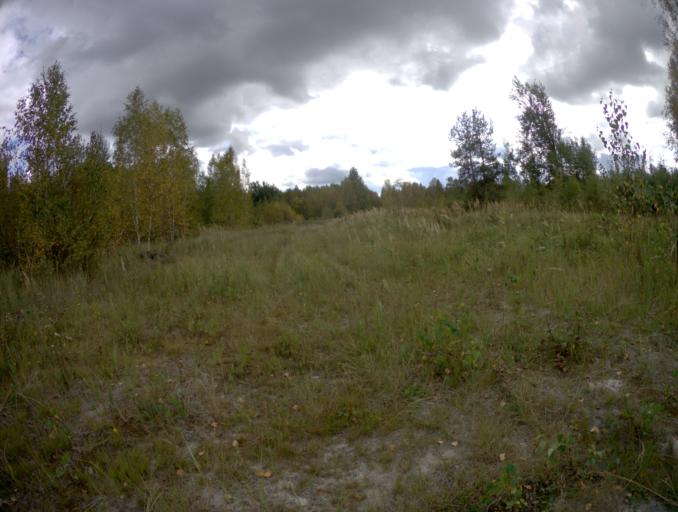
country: RU
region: Vladimir
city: Urshel'skiy
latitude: 55.7765
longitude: 40.1465
